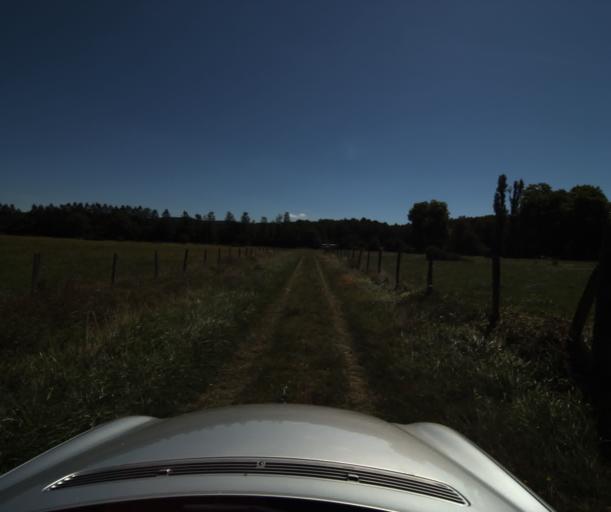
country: FR
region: Languedoc-Roussillon
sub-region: Departement de l'Aude
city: Chalabre
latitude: 42.9884
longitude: 1.9278
